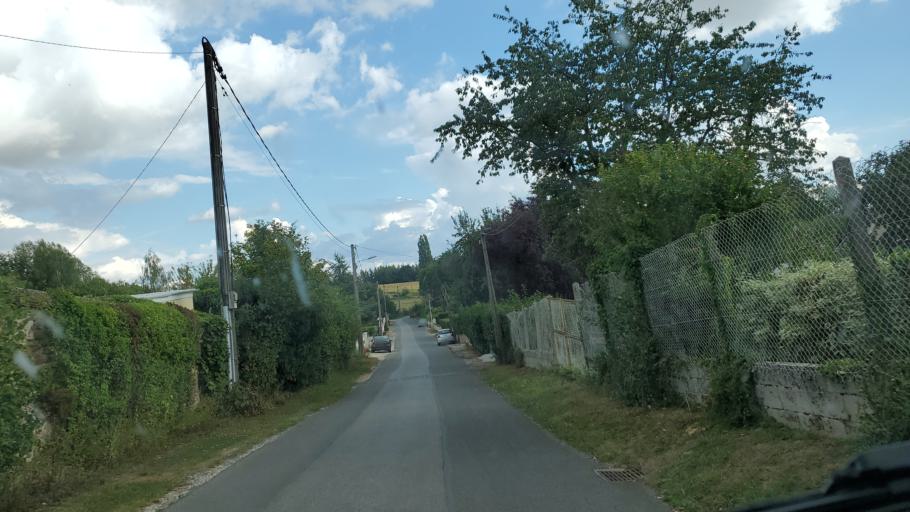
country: FR
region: Ile-de-France
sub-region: Departement de Seine-et-Marne
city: Chailly-en-Brie
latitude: 48.7761
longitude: 3.1639
